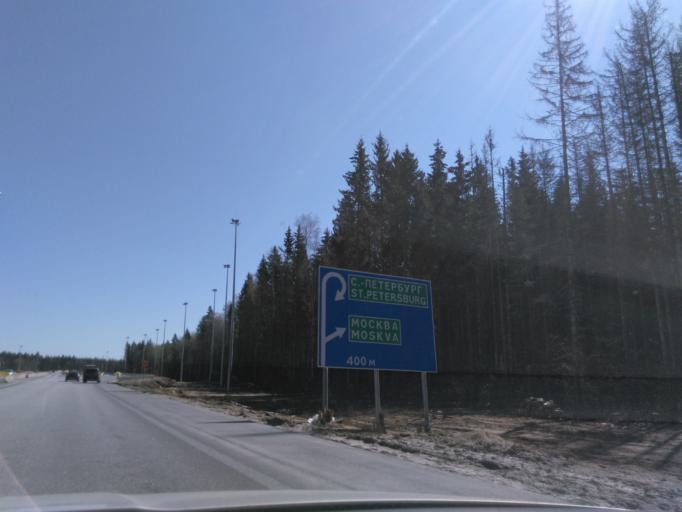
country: RU
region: Moskovskaya
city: Rzhavki
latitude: 56.0040
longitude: 37.2633
